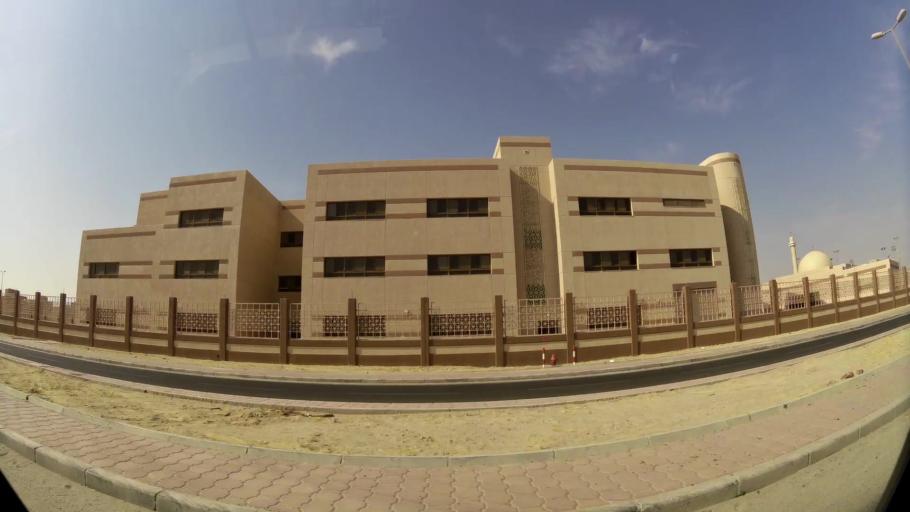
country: KW
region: Al Ahmadi
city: Al Wafrah
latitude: 28.7989
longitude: 48.0714
